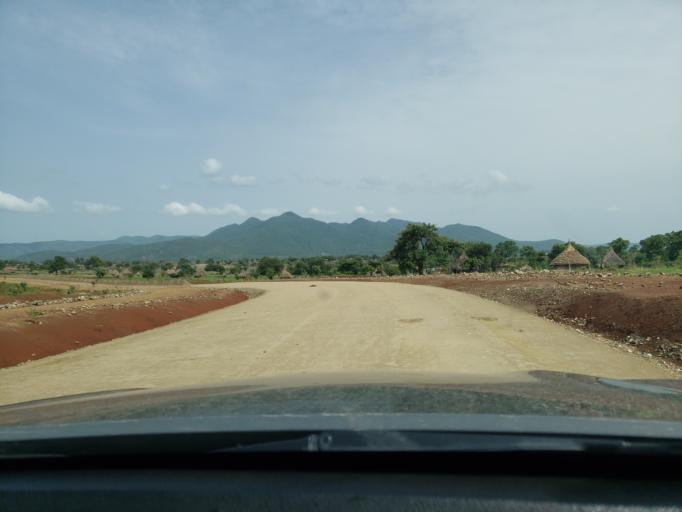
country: ET
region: Oromiya
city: Mendi
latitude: 10.1216
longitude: 35.1504
